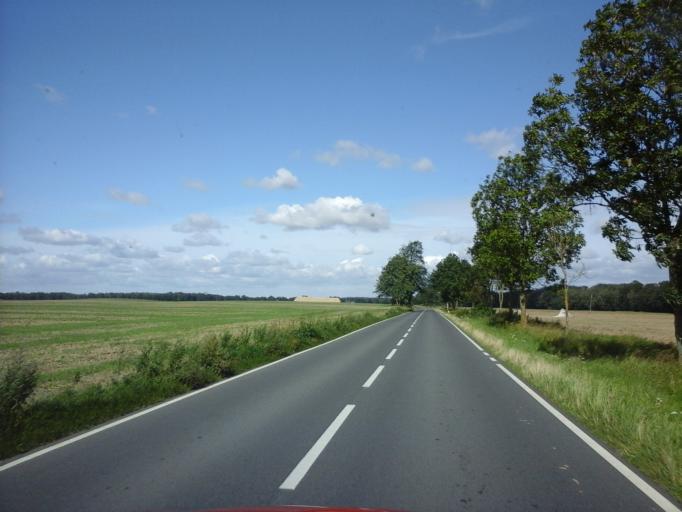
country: PL
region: West Pomeranian Voivodeship
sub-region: Powiat stargardzki
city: Dolice
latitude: 53.1988
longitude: 15.1721
